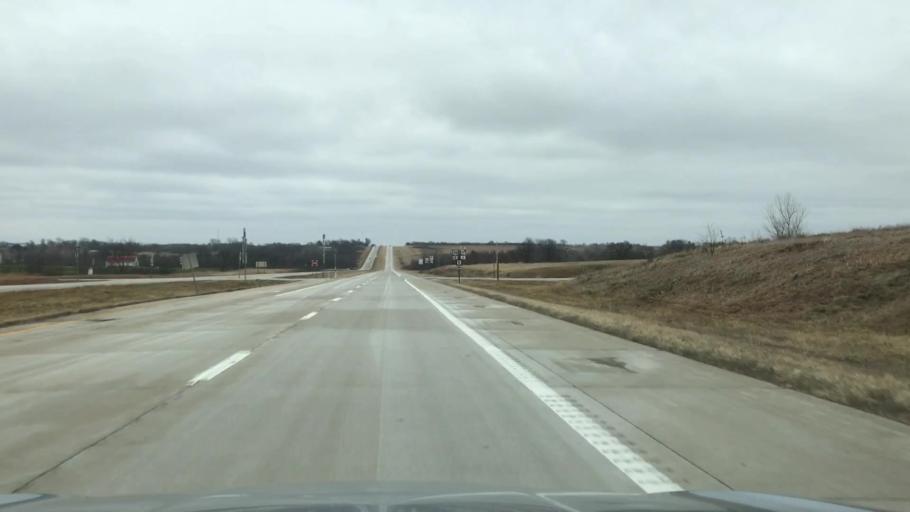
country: US
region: Missouri
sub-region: Livingston County
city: Chillicothe
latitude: 39.7374
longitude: -93.7099
